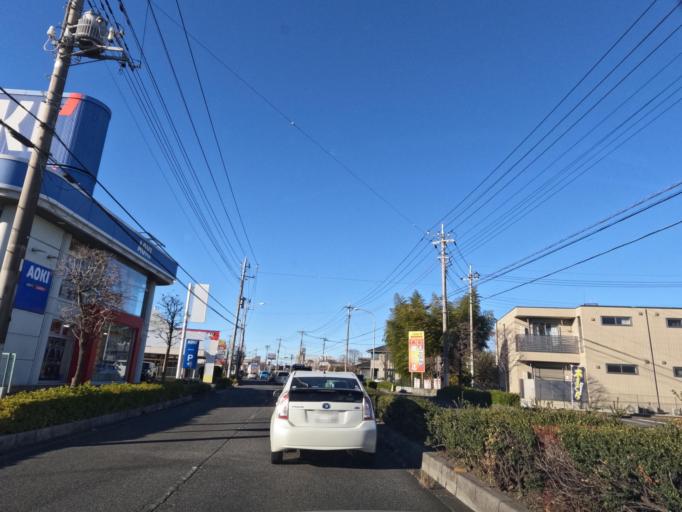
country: JP
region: Saitama
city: Hasuda
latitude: 35.9403
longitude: 139.6450
